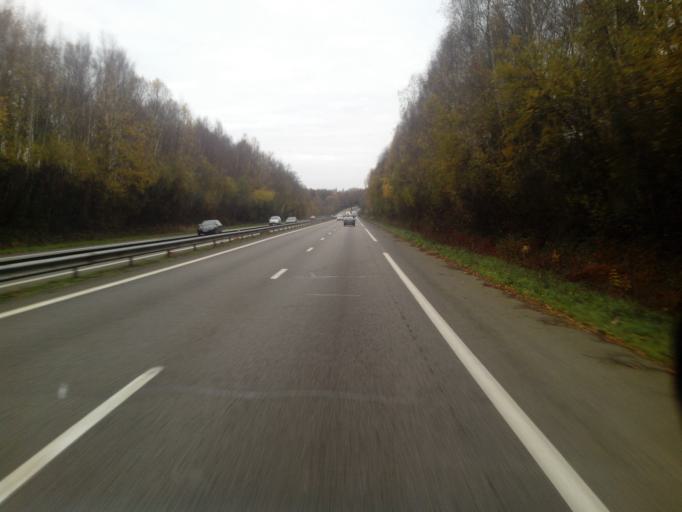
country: FR
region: Pays de la Loire
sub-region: Departement de la Loire-Atlantique
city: Treillieres
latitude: 47.3284
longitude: -1.6488
